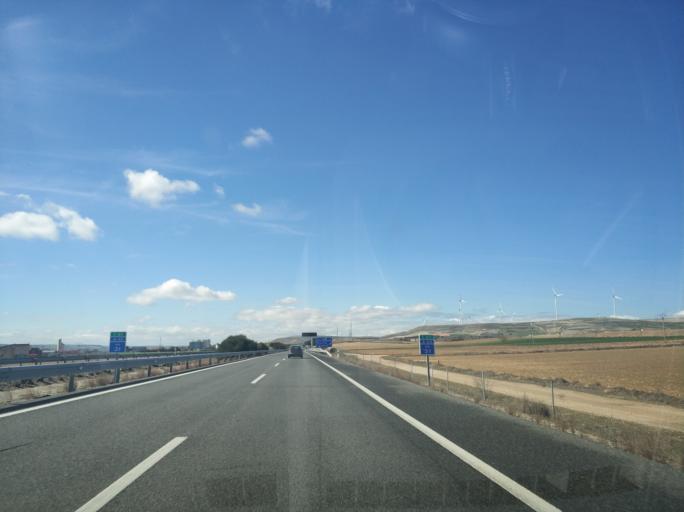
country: ES
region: Castille and Leon
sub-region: Provincia de Burgos
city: Villaquiran de los Infantes
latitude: 42.2287
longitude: -3.9930
